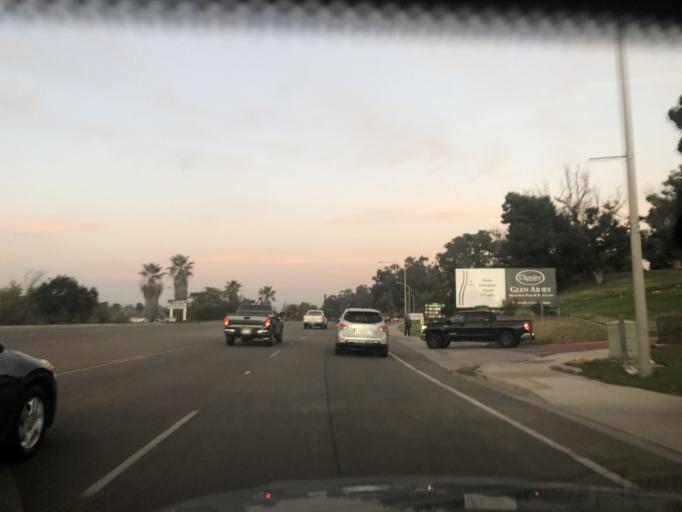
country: US
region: California
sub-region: San Diego County
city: Bonita
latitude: 32.6529
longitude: -117.0484
